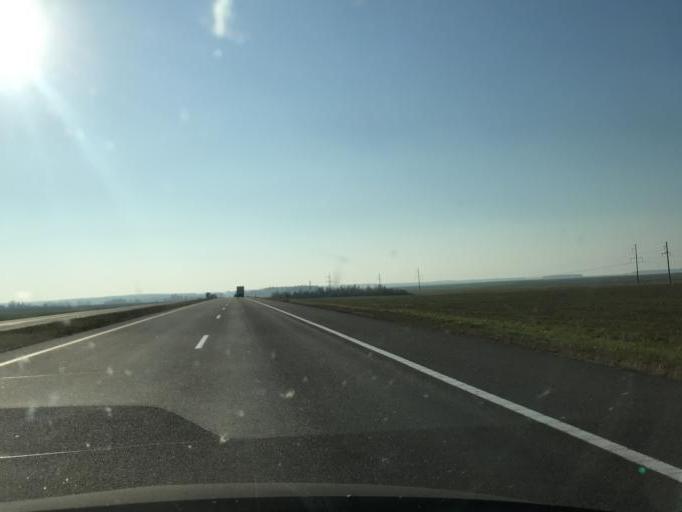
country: BY
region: Minsk
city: Haradzyeya
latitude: 53.3999
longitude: 26.5436
